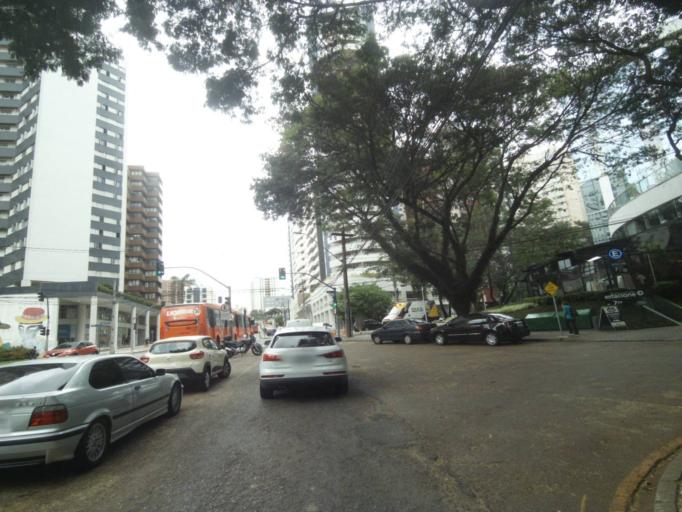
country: BR
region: Parana
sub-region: Curitiba
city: Curitiba
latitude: -25.4488
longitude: -49.2880
